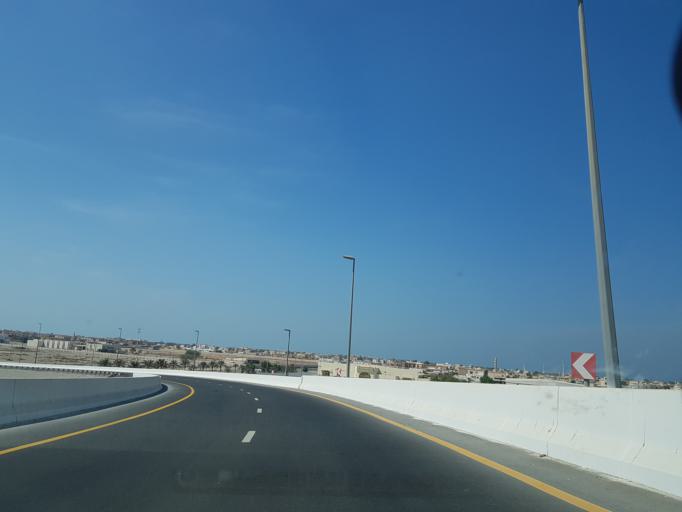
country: AE
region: Ra's al Khaymah
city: Ras al-Khaimah
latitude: 25.8337
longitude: 56.0158
